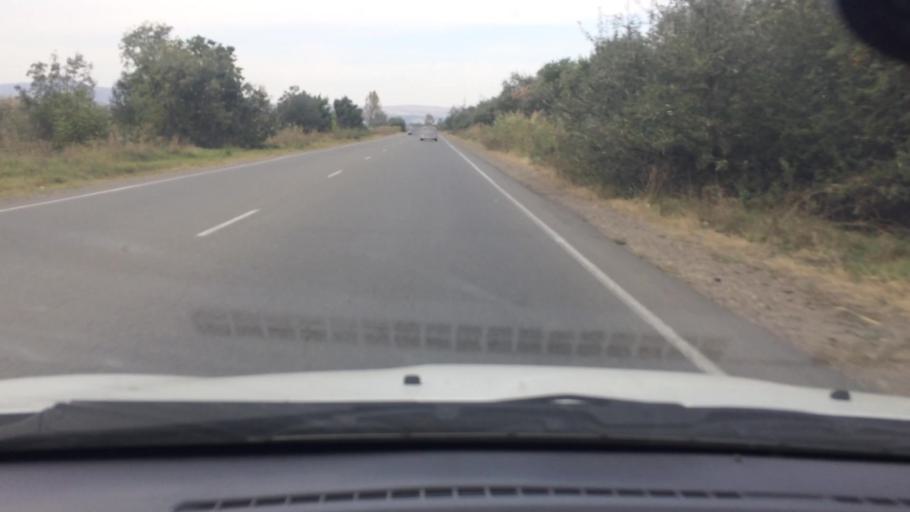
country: GE
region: Kvemo Kartli
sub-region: Marneuli
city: Marneuli
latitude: 41.5324
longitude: 44.7770
